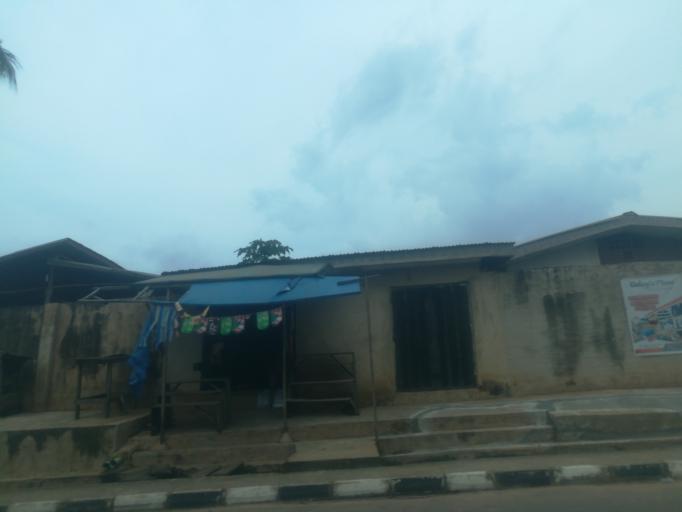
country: NG
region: Oyo
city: Ibadan
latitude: 7.3693
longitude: 3.8283
